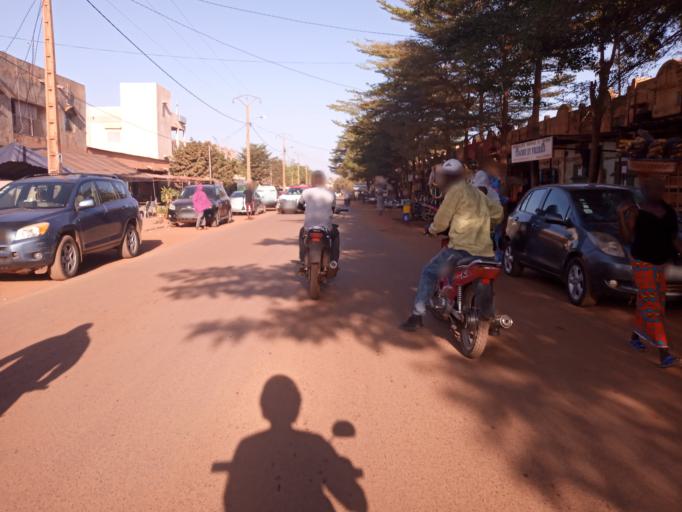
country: ML
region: Bamako
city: Bamako
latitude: 12.6115
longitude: -7.9554
